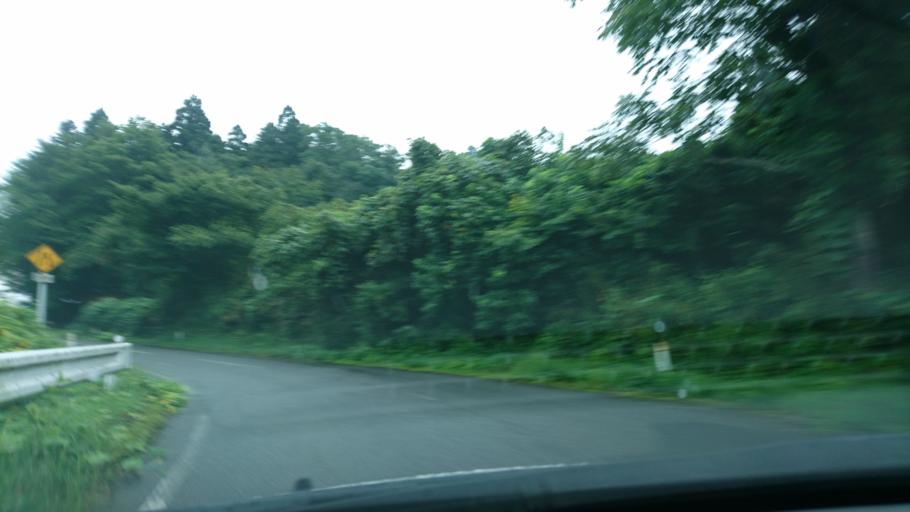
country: JP
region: Iwate
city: Ichinoseki
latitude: 38.8795
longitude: 141.2558
